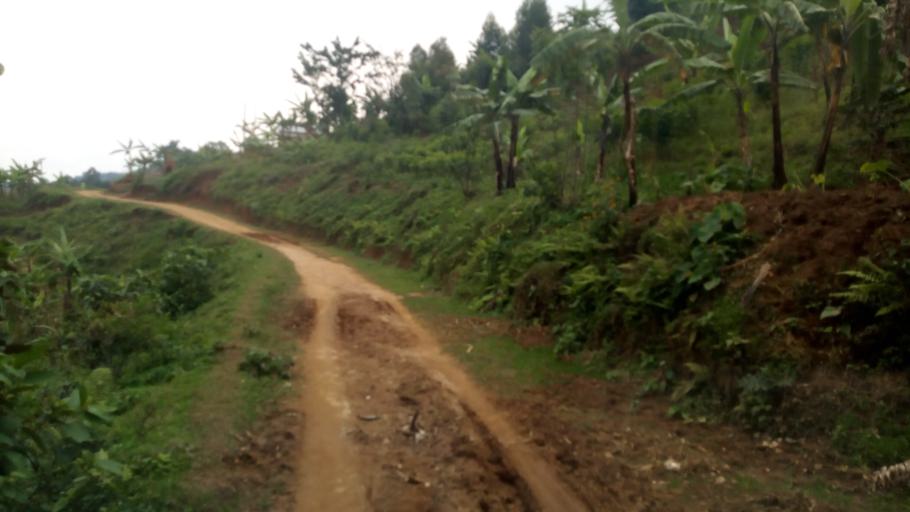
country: UG
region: Western Region
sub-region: Kisoro District
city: Kisoro
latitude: -1.2394
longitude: 29.6149
